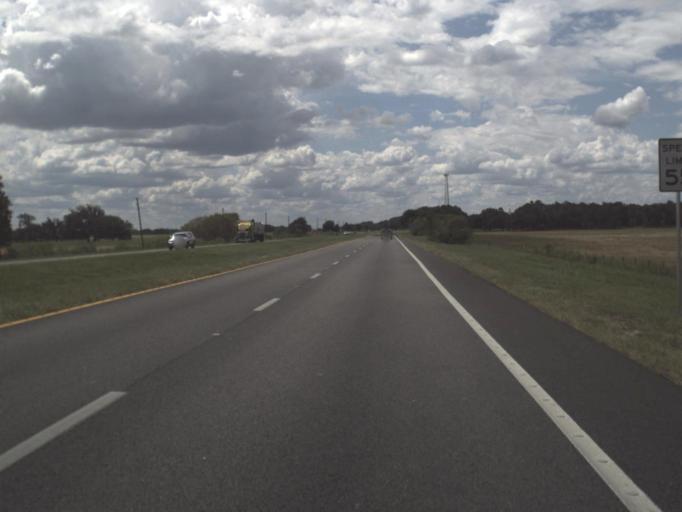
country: US
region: Florida
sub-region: Polk County
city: Alturas
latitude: 27.9136
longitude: -81.6994
